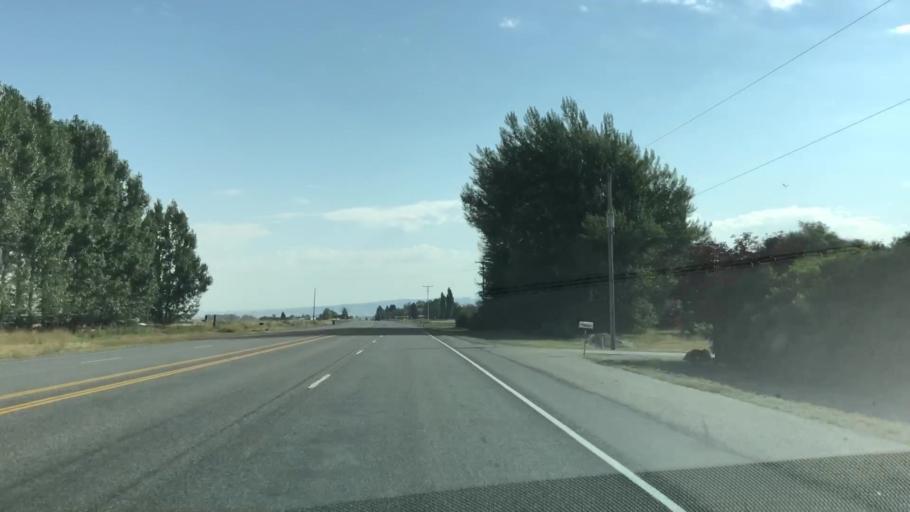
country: US
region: Idaho
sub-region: Jefferson County
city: Rigby
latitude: 43.6013
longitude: -111.8520
